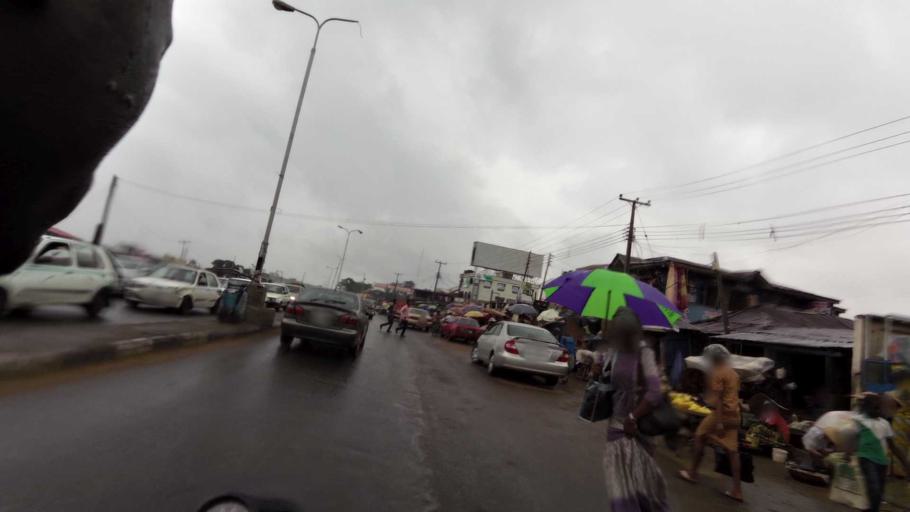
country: NG
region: Oyo
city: Ibadan
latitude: 7.4223
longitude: 3.8979
